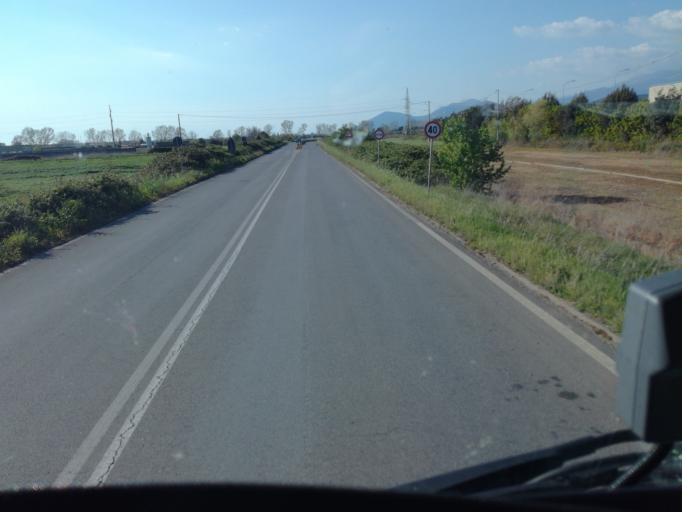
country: IT
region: Latium
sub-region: Provincia di Latina
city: Priverno
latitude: 41.4068
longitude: 13.1629
